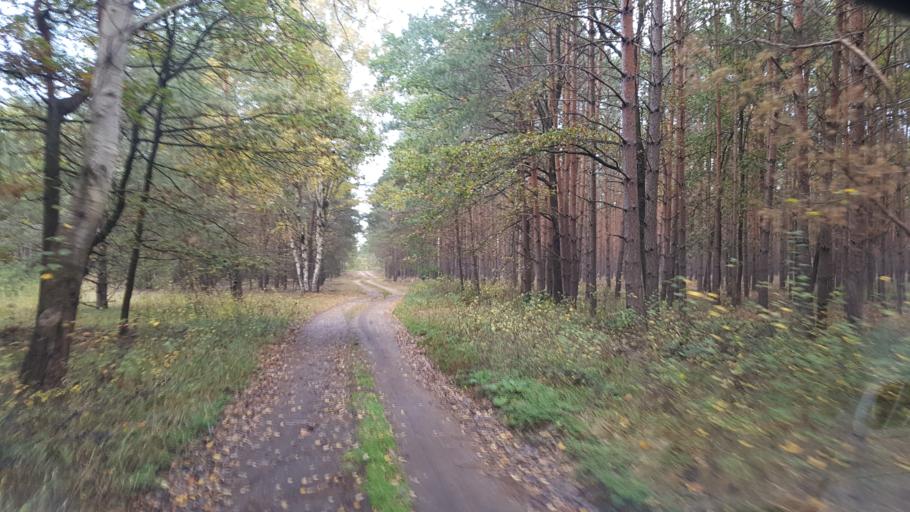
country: DE
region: Brandenburg
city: Schonborn
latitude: 51.6524
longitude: 13.5080
